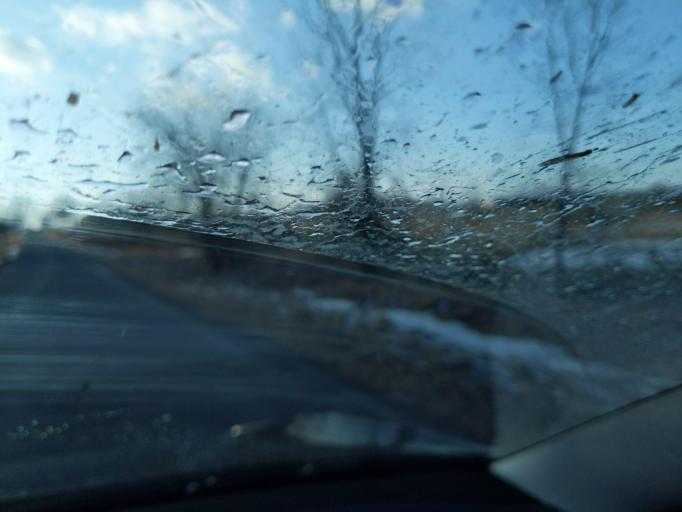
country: US
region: Michigan
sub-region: Ingham County
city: Stockbridge
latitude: 42.5185
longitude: -84.1869
